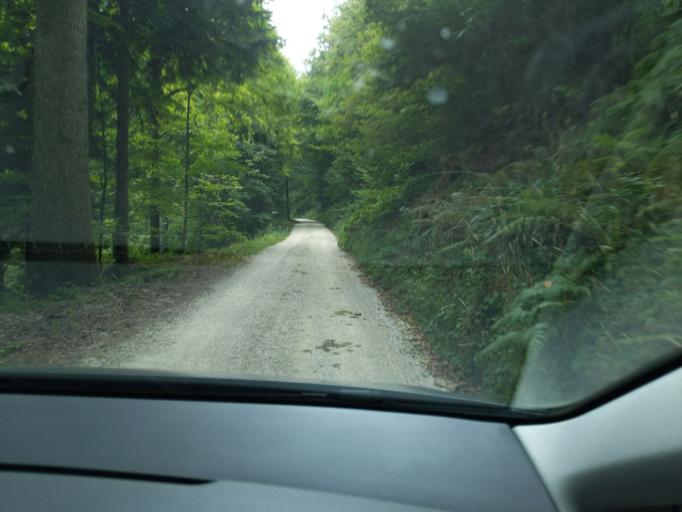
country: CH
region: Bern
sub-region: Oberaargau
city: Wyssachen
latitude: 47.0309
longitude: 7.8303
